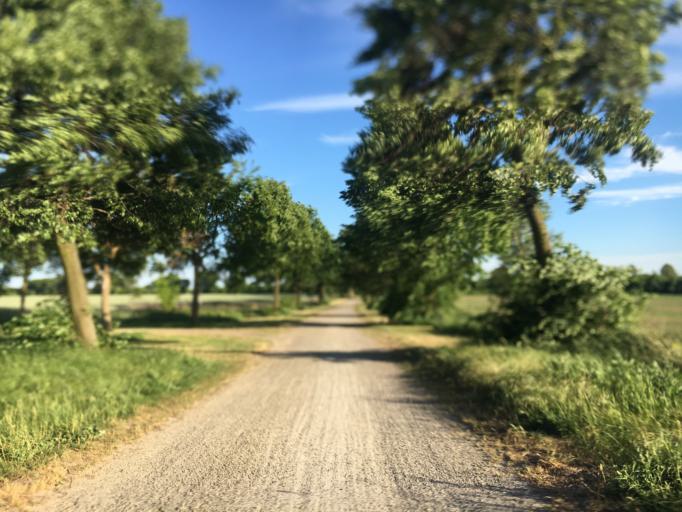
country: DE
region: Brandenburg
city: Potsdam
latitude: 52.4309
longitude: 13.0248
